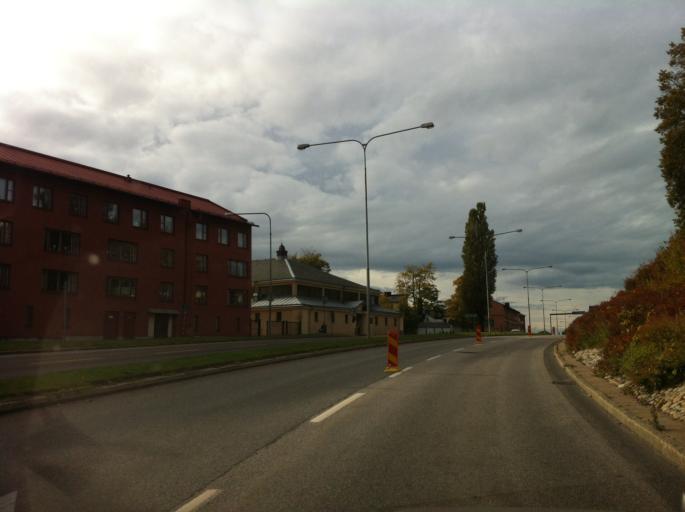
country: SE
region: OEstergoetland
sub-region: Motala Kommun
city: Motala
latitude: 58.5370
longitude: 15.0433
